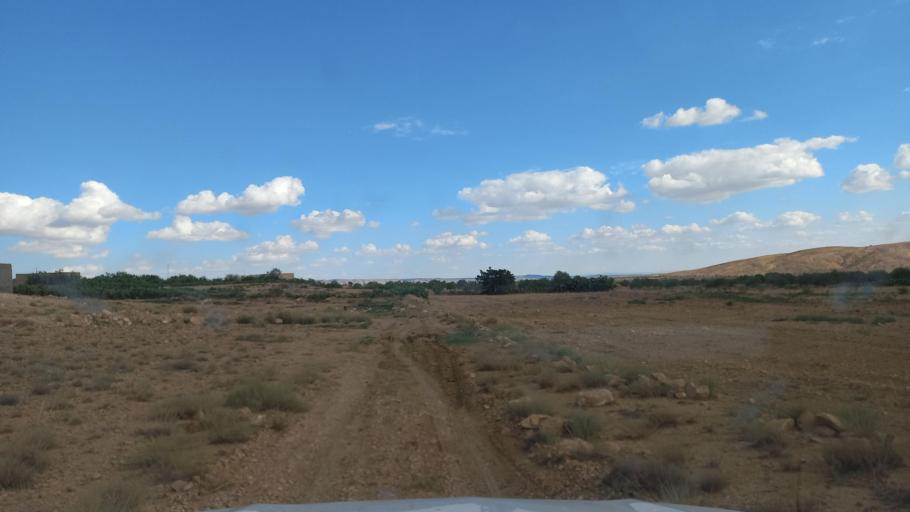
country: TN
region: Al Qasrayn
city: Sbiba
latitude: 35.4028
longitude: 9.0119
